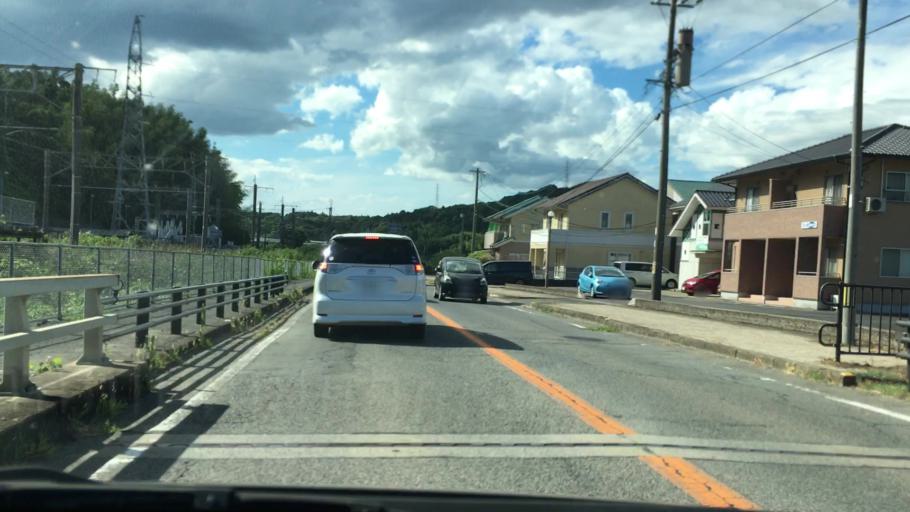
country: JP
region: Saga Prefecture
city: Takeocho-takeo
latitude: 33.1940
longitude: 129.9802
